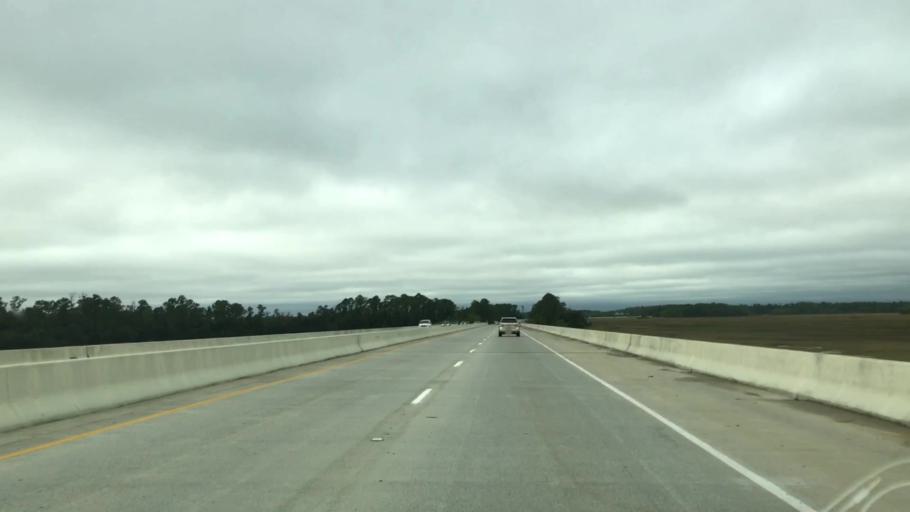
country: US
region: South Carolina
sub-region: Beaufort County
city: Shell Point
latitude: 32.3786
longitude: -80.7923
